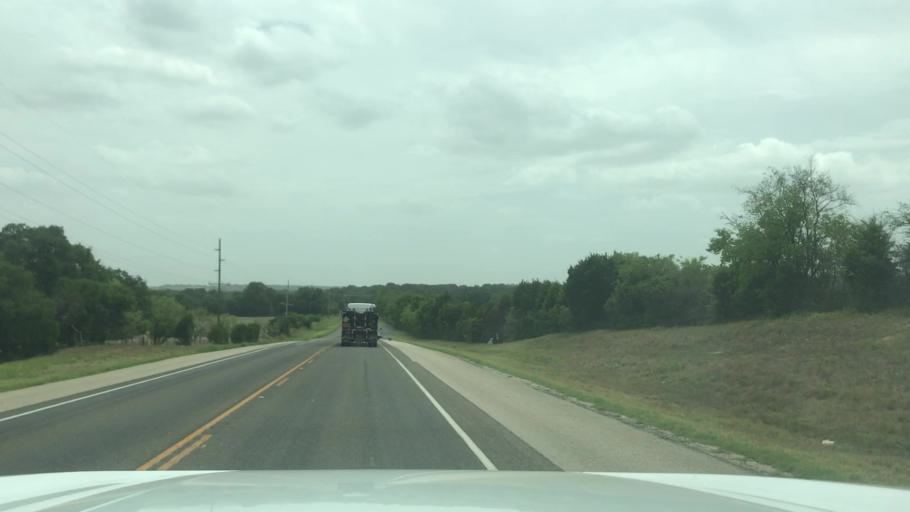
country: US
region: Texas
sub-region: Bosque County
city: Valley Mills
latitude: 31.6848
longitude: -97.5287
